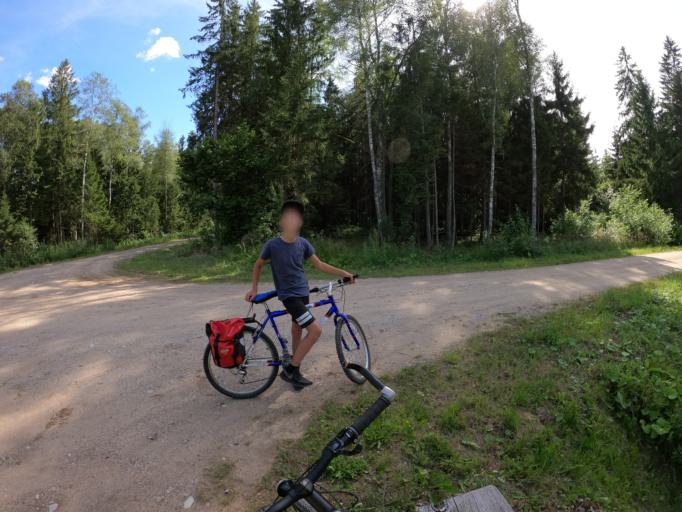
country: LT
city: Tytuveneliai
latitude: 55.6883
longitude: 23.1921
